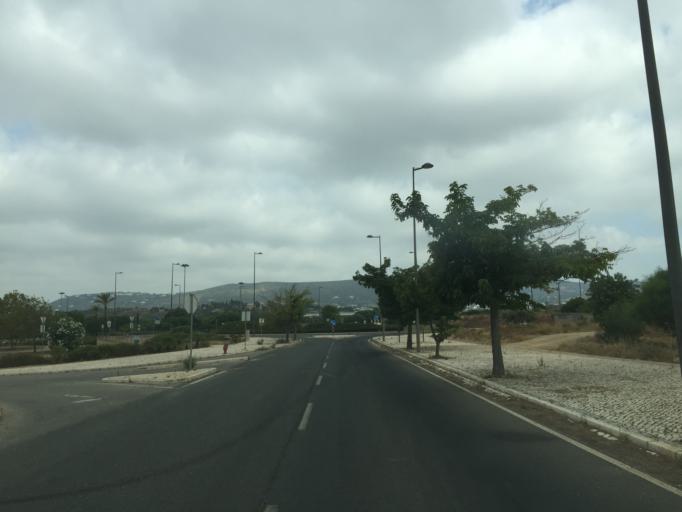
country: PT
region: Faro
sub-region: Faro
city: Santa Barbara de Nexe
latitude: 37.0852
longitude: -7.9786
